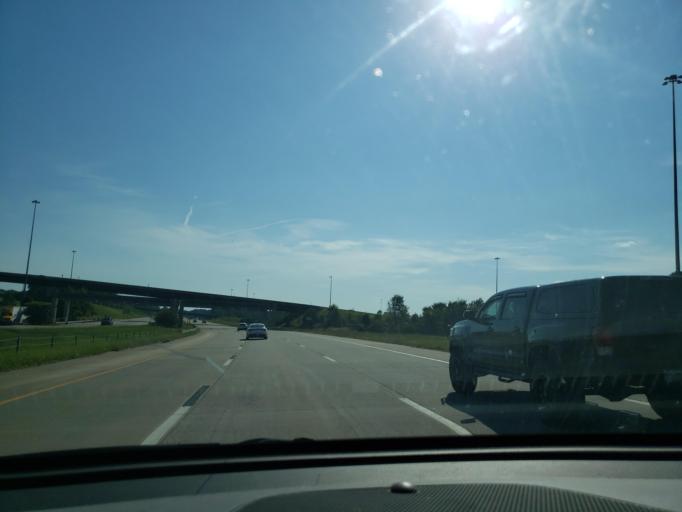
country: US
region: North Carolina
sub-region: Wake County
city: Morrisville
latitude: 35.8593
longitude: -78.8558
